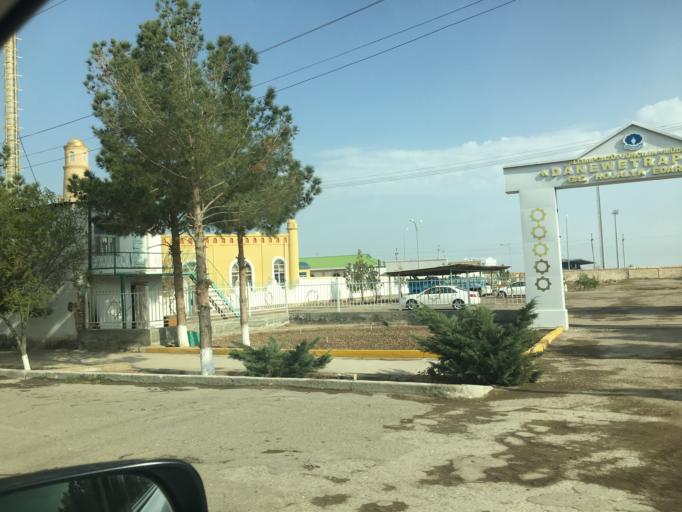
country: TM
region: Mary
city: Seydi
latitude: 39.2643
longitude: 63.1799
